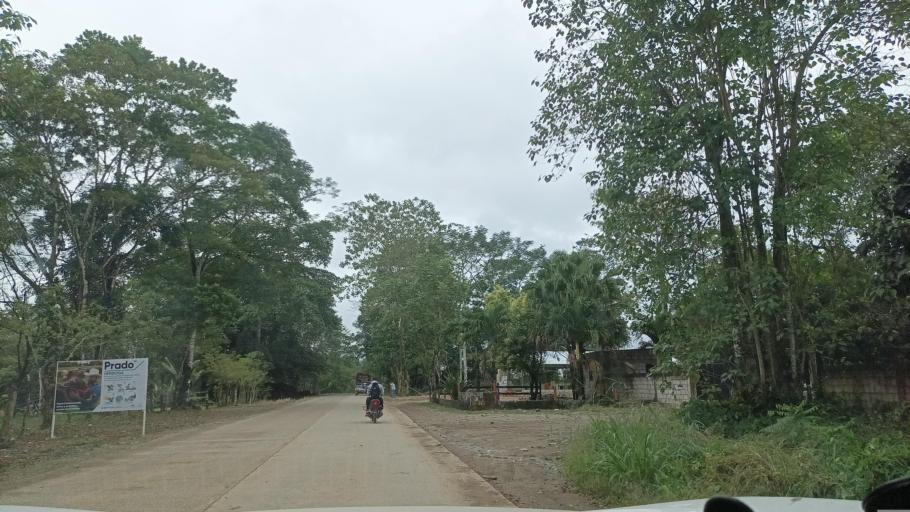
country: MX
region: Veracruz
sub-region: Uxpanapa
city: Poblado 10
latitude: 17.2780
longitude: -94.4713
